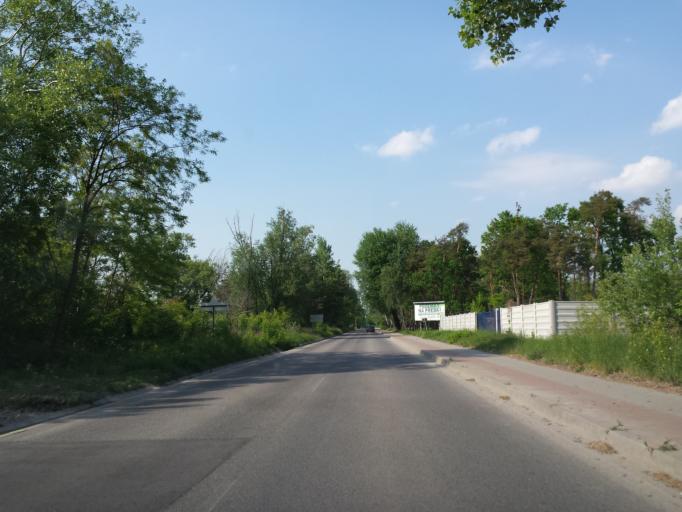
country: SK
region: Bratislavsky
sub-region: Okres Malacky
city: Malacky
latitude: 48.4159
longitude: 17.0207
